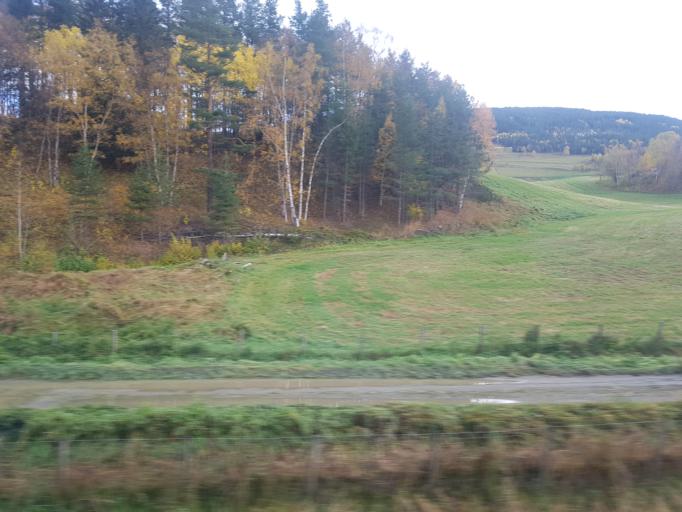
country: NO
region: Oppland
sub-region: Dovre
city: Dovre
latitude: 61.9767
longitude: 9.2602
